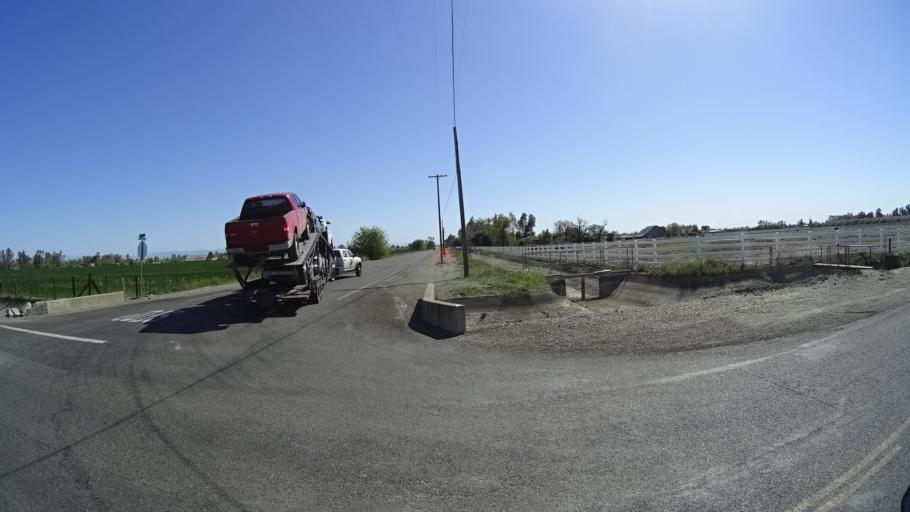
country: US
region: California
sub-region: Glenn County
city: Orland
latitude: 39.7404
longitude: -122.2157
